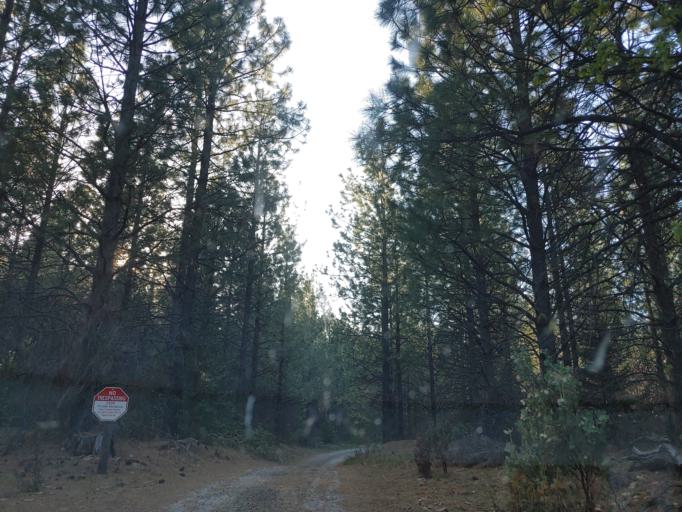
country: US
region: California
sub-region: Shasta County
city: Burney
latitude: 40.8119
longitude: -121.9470
